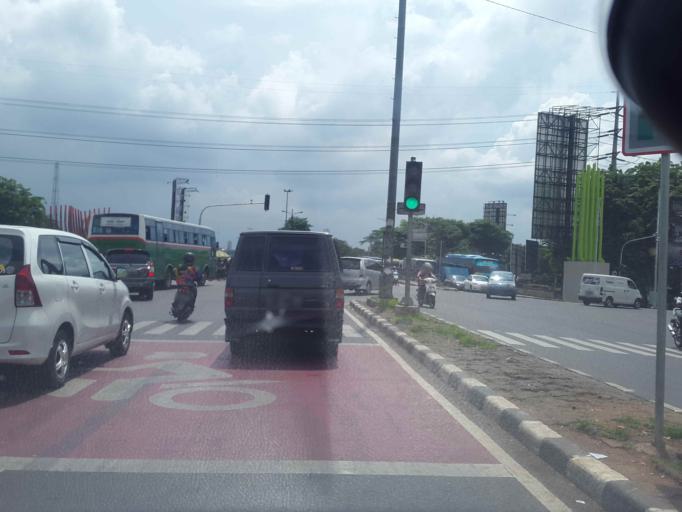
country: ID
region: West Java
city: Bekasi
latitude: -6.2605
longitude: 107.0194
